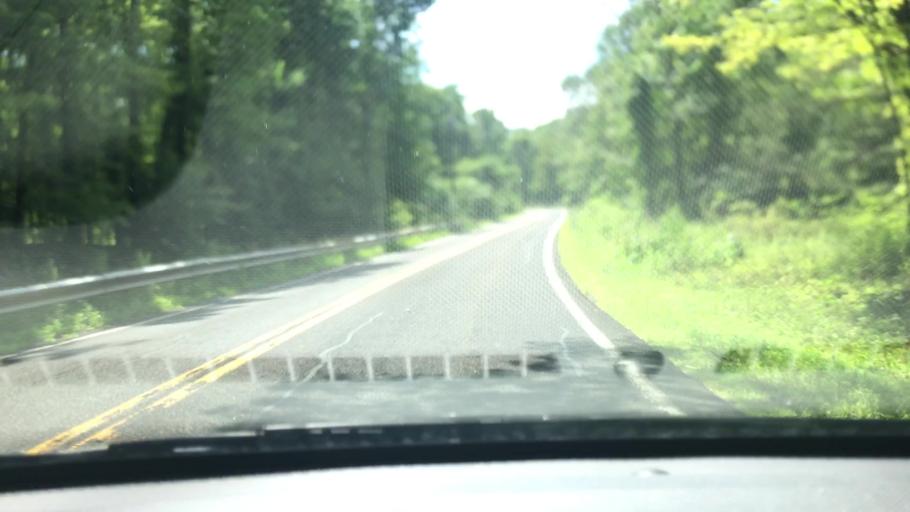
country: US
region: New York
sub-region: Ulster County
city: Stone Ridge
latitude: 41.8976
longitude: -74.1632
